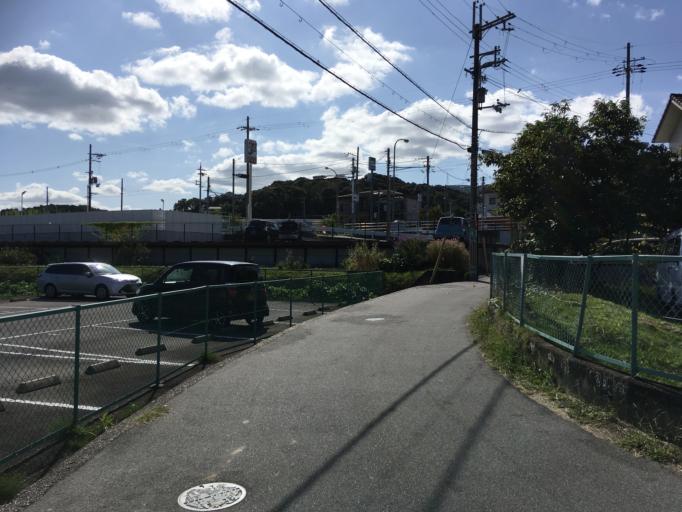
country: JP
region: Nara
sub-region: Ikoma-shi
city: Ikoma
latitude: 34.6749
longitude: 135.7070
